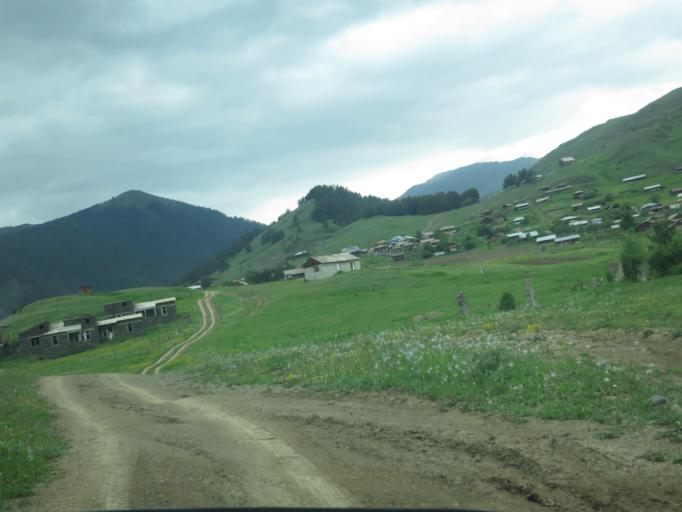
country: RU
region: Chechnya
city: Itum-Kali
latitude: 42.3674
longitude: 45.6400
